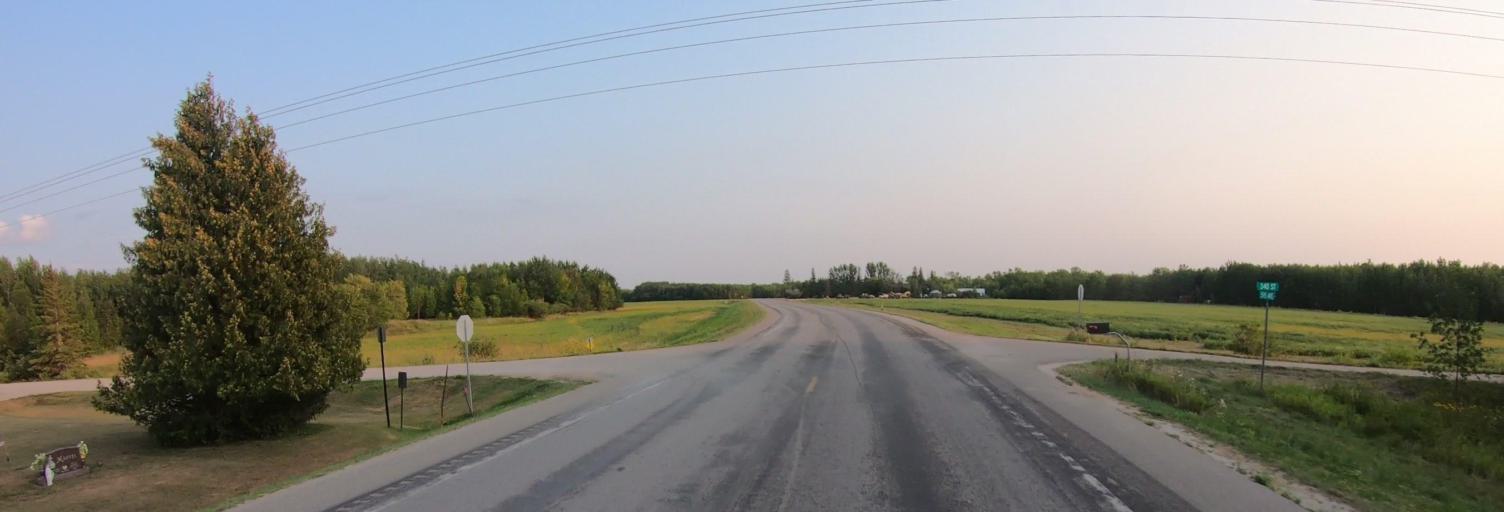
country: US
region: Minnesota
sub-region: Roseau County
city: Warroad
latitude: 48.8872
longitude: -95.3202
